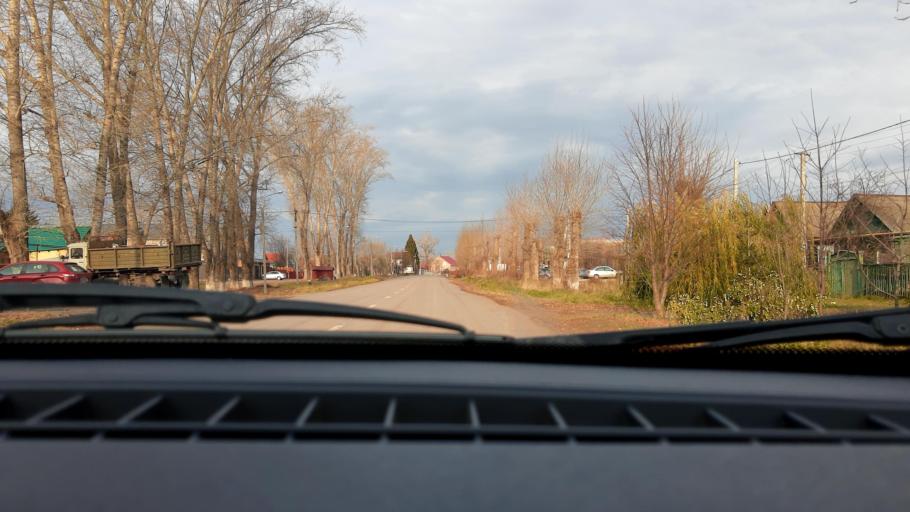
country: RU
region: Bashkortostan
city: Mikhaylovka
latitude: 54.7592
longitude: 55.9039
